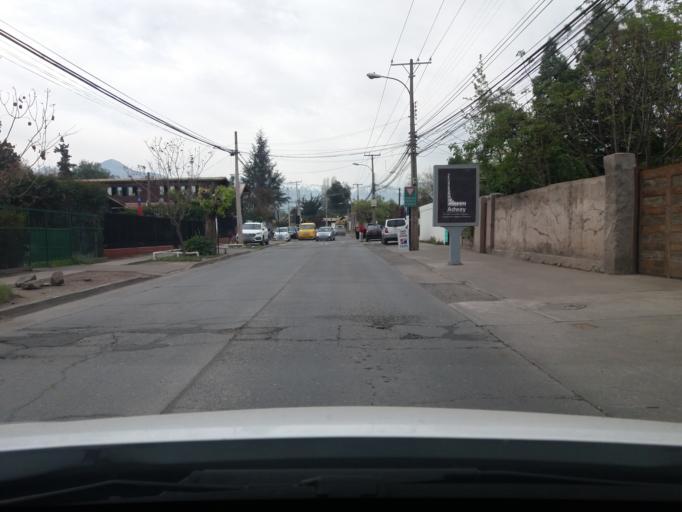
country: CL
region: Valparaiso
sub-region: Provincia de Los Andes
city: Los Andes
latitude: -32.8316
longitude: -70.6099
